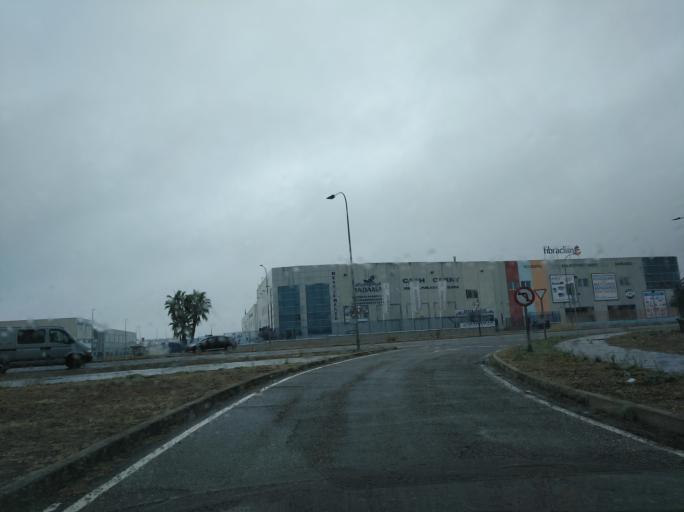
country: ES
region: Extremadura
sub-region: Provincia de Badajoz
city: Badajoz
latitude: 38.8984
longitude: -6.9907
